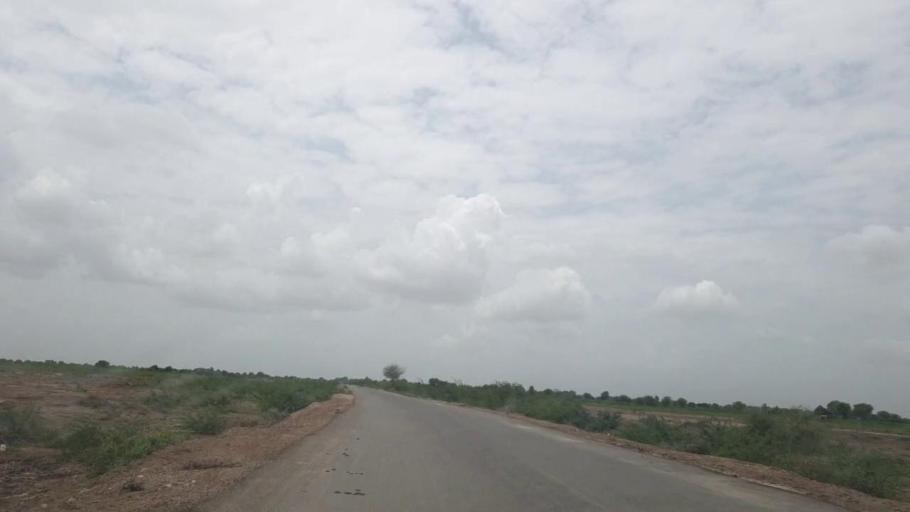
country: PK
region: Sindh
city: Naukot
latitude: 24.9454
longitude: 69.2800
